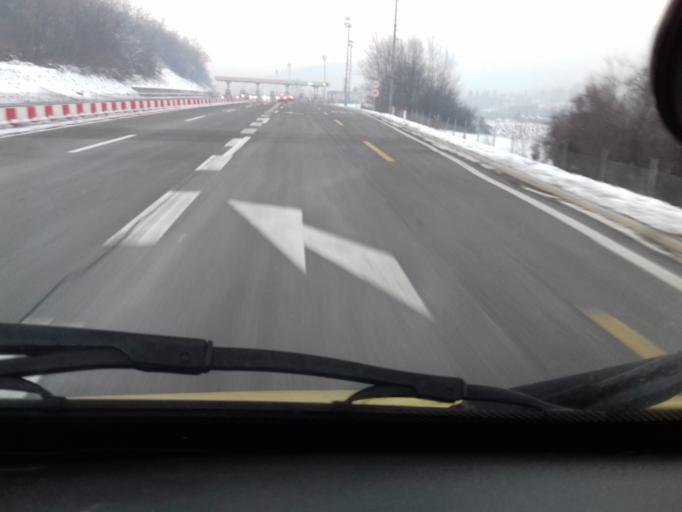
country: BA
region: Federation of Bosnia and Herzegovina
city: Vogosca
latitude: 43.9096
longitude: 18.3223
